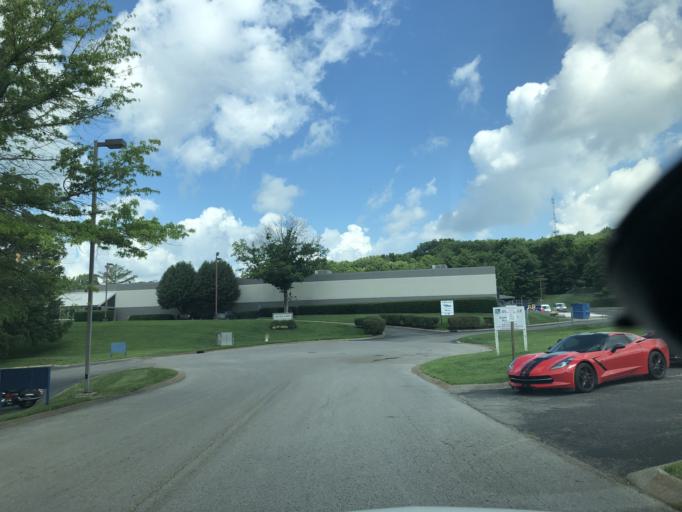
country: US
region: Tennessee
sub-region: Rutherford County
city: La Vergne
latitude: 36.0192
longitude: -86.6238
